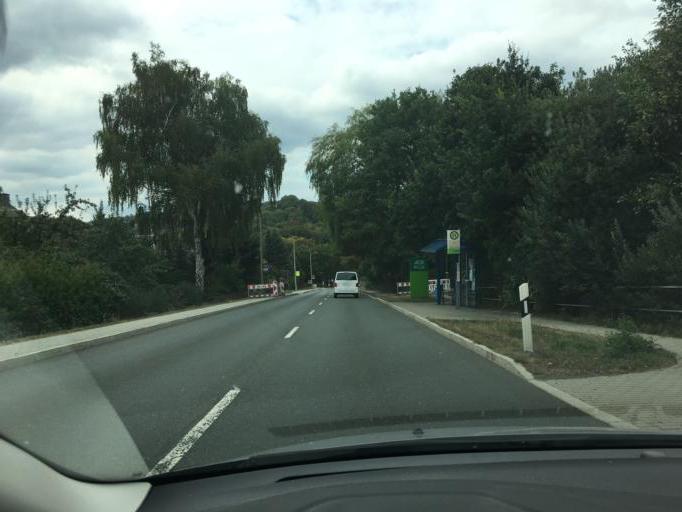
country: DE
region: Thuringia
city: Bad Lobenstein
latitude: 50.4513
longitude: 11.6472
